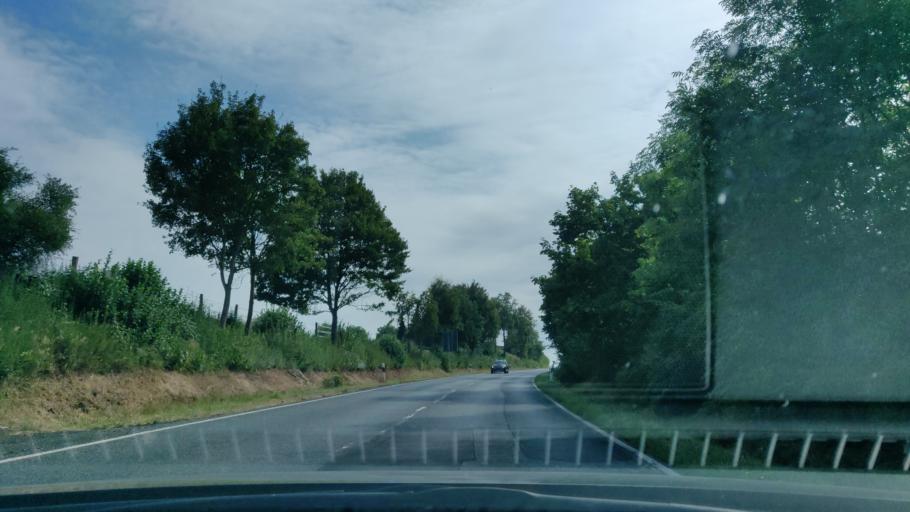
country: DE
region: Hesse
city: Fritzlar
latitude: 51.1376
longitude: 9.2600
